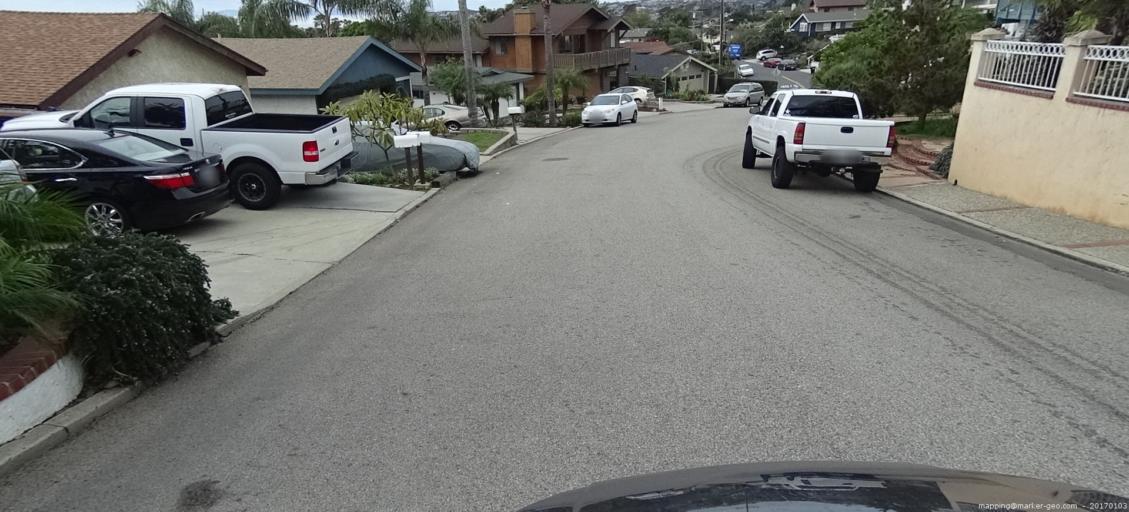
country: US
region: California
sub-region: Orange County
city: San Juan Capistrano
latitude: 33.4629
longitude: -117.6557
